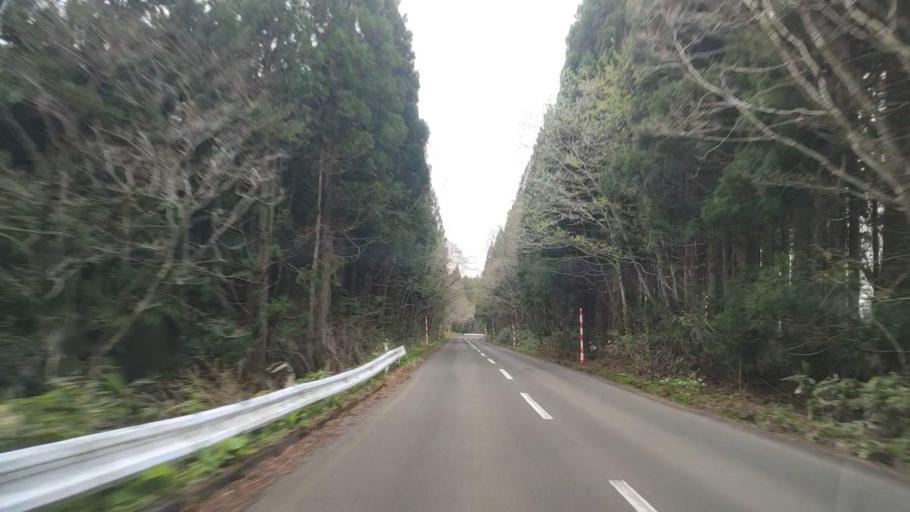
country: JP
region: Akita
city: Hanawa
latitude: 40.3923
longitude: 140.7951
